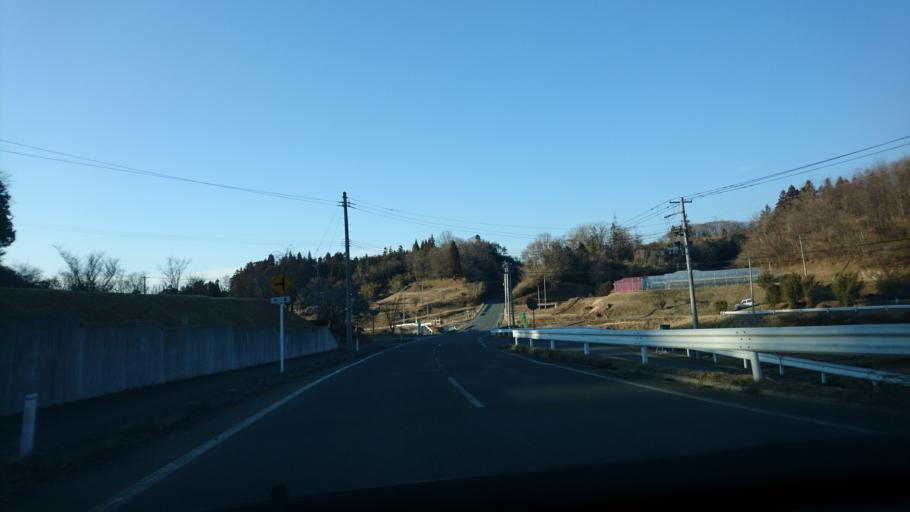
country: JP
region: Iwate
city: Ichinoseki
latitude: 38.9314
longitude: 141.3596
